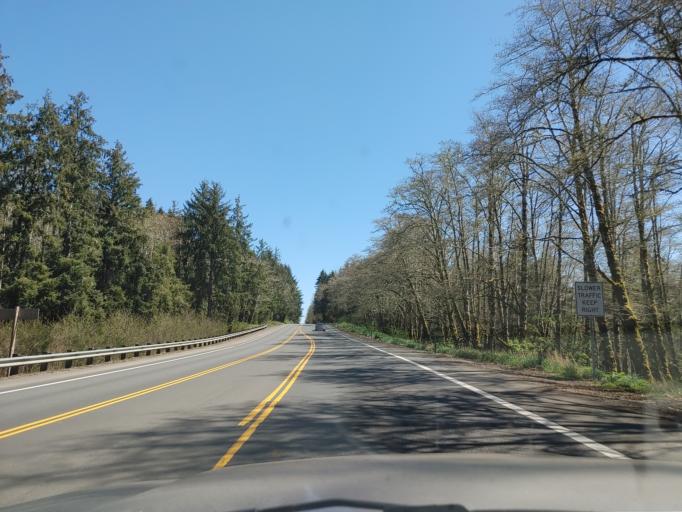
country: US
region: Oregon
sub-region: Clatsop County
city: Warrenton
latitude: 46.1443
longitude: -123.8988
